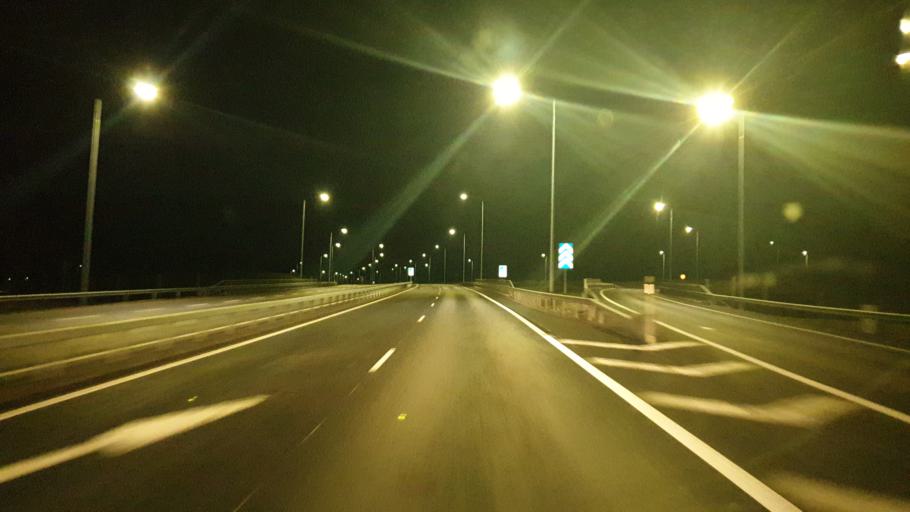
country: FI
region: Central Finland
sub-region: AEaenekoski
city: AEaenekoski
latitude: 62.6081
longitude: 25.6894
